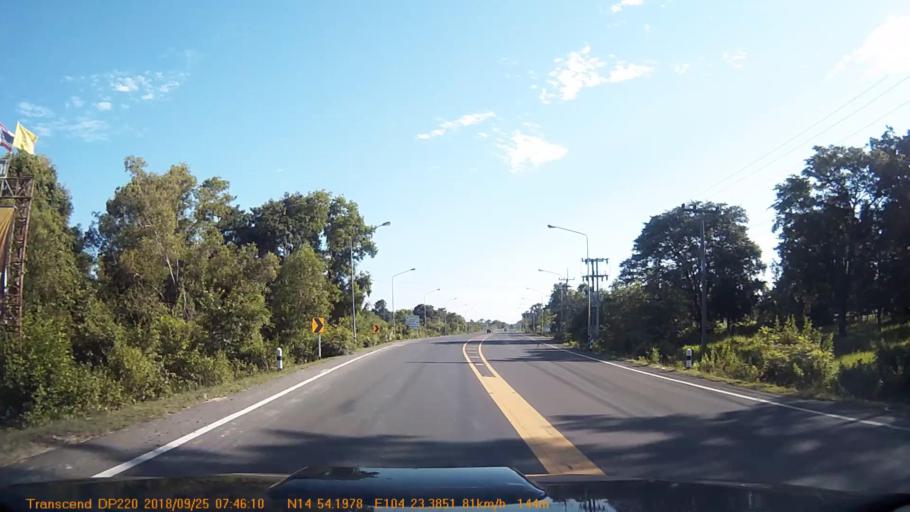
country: TH
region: Sisaket
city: Phayu
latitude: 14.9036
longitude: 104.3898
